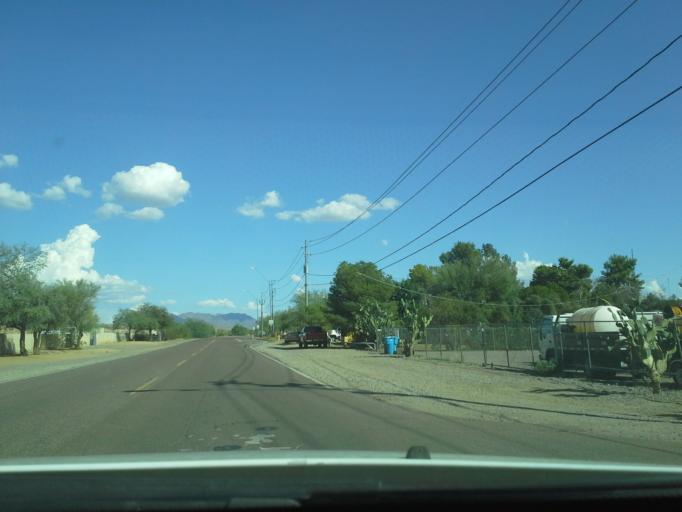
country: US
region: Arizona
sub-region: Maricopa County
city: Paradise Valley
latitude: 33.6769
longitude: -112.0224
